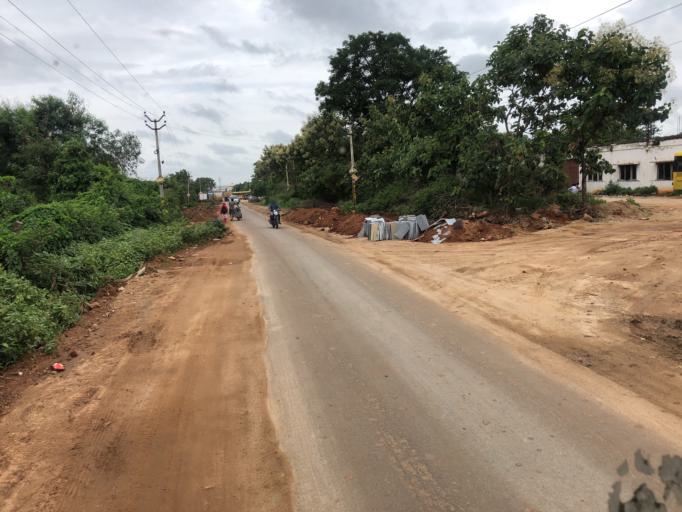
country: IN
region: Telangana
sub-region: Medak
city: Serilingampalle
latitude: 17.4250
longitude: 78.2960
